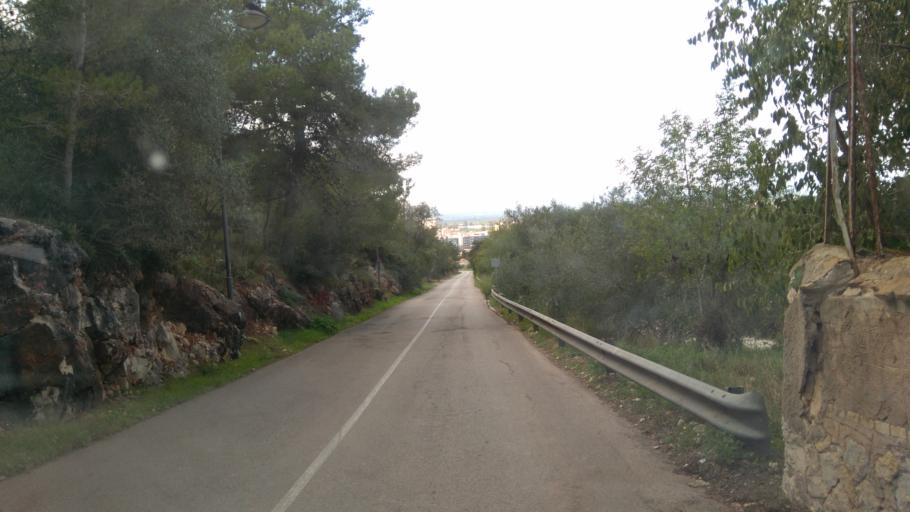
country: ES
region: Valencia
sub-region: Provincia de Valencia
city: Alzira
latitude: 39.1536
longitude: -0.4179
